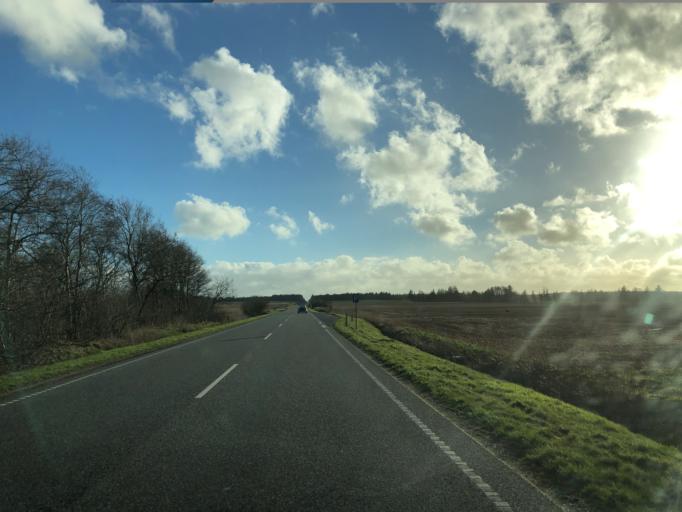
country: DK
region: Central Jutland
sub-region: Herning Kommune
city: Vildbjerg
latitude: 56.1884
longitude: 8.7082
